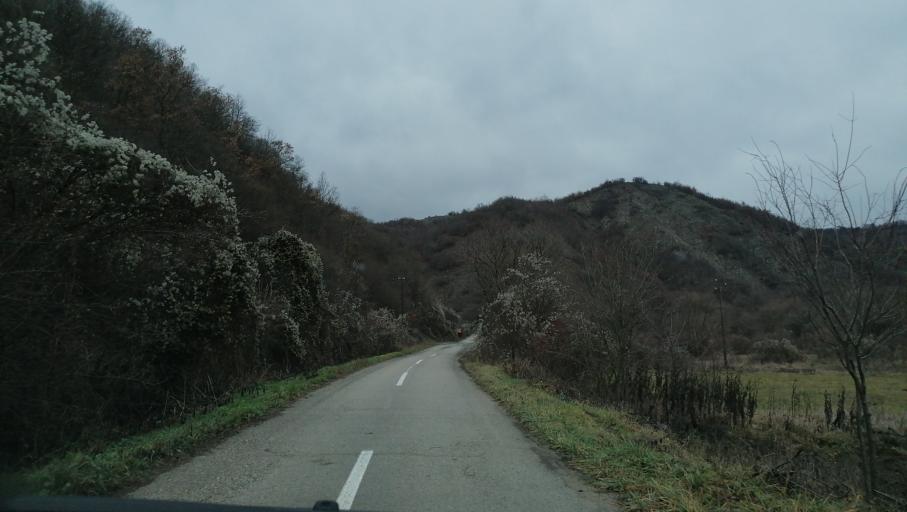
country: RS
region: Central Serbia
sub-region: Pirotski Okrug
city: Dimitrovgrad
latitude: 42.9459
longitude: 22.7674
